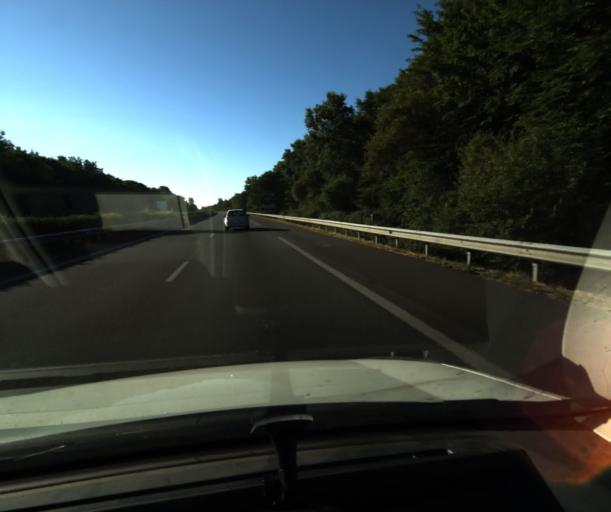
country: FR
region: Midi-Pyrenees
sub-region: Departement du Tarn-et-Garonne
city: Montech
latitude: 43.9923
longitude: 1.2333
